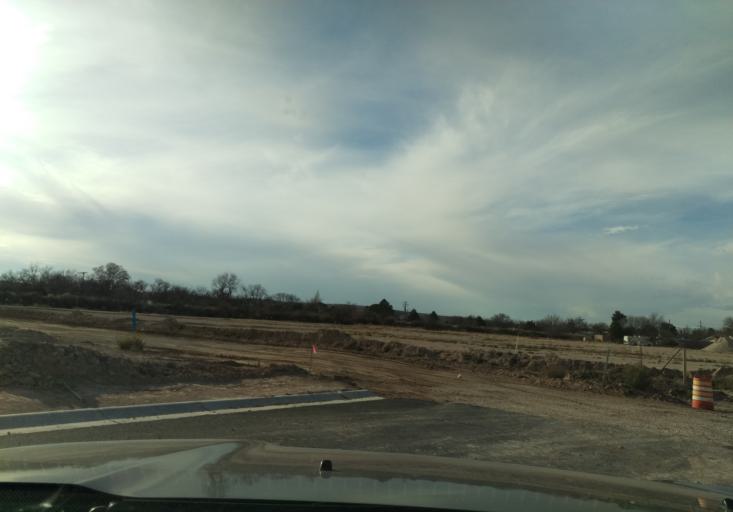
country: US
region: New Mexico
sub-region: Eddy County
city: La Huerta
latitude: 32.4489
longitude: -104.2417
